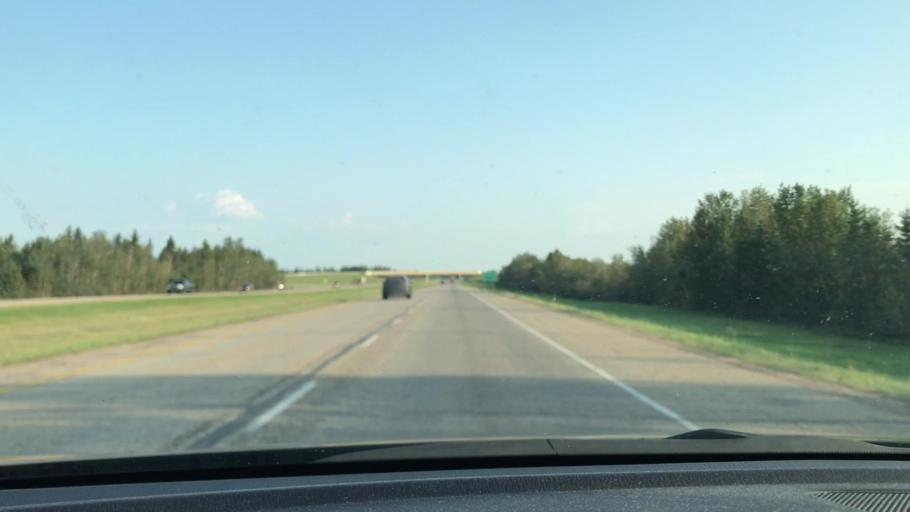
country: CA
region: Alberta
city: Lacombe
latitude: 52.5646
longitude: -113.6630
